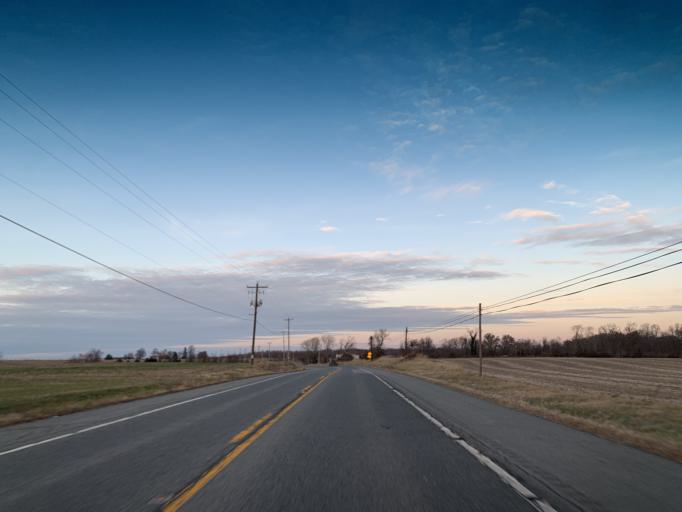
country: US
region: Delaware
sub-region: New Castle County
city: Middletown
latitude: 39.4147
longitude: -75.8622
